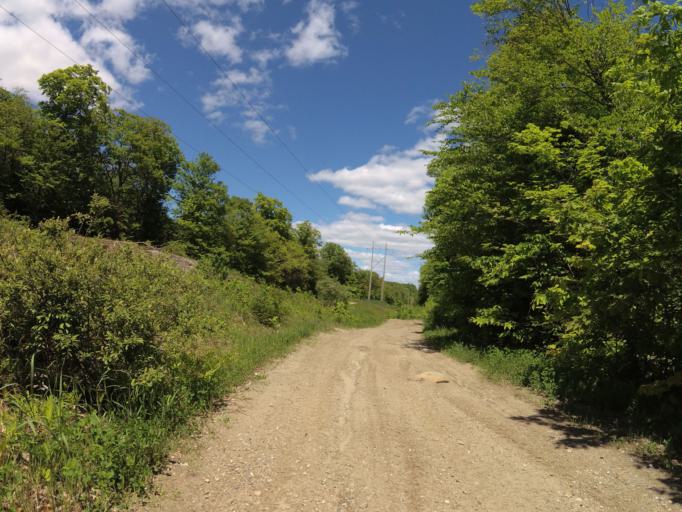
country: CA
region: Ontario
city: Renfrew
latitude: 45.0150
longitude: -76.8955
